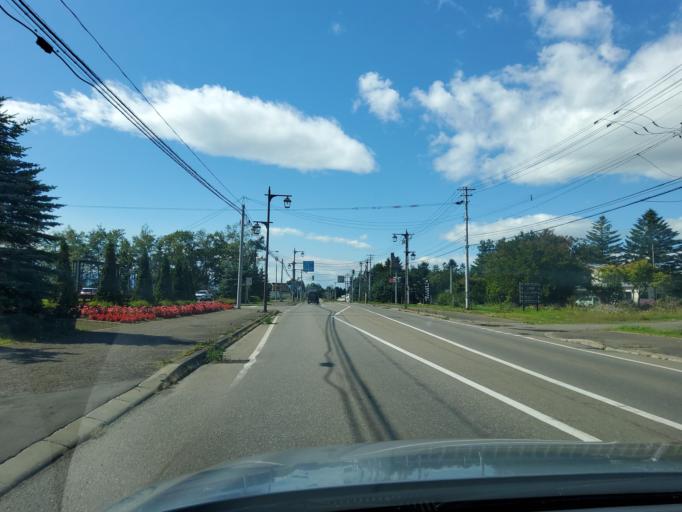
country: JP
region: Hokkaido
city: Obihiro
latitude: 42.9346
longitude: 143.2966
